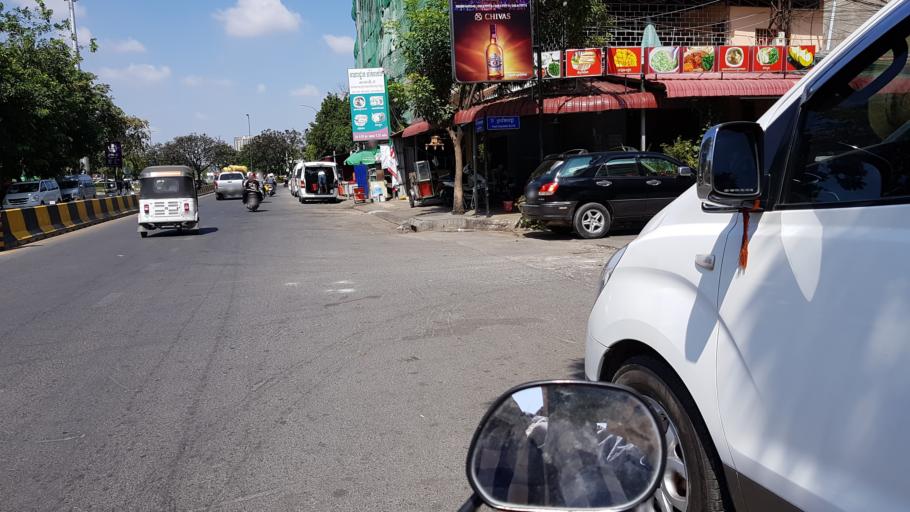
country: KH
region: Phnom Penh
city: Phnom Penh
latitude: 11.5694
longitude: 104.9111
